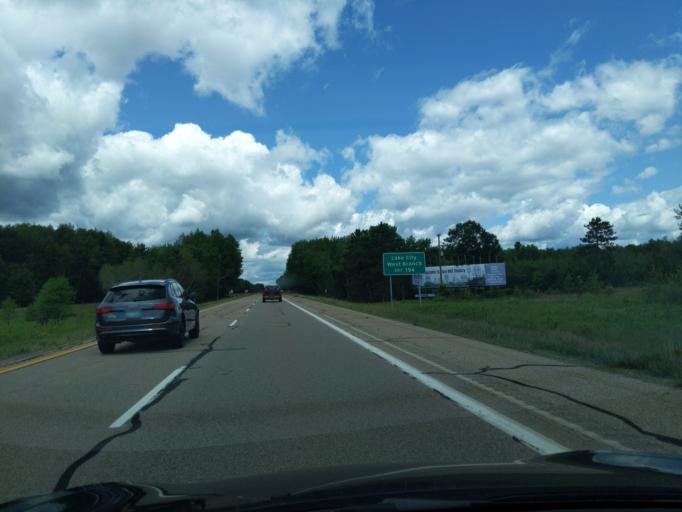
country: US
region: Michigan
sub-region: Roscommon County
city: Houghton Lake
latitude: 44.3194
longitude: -84.8063
